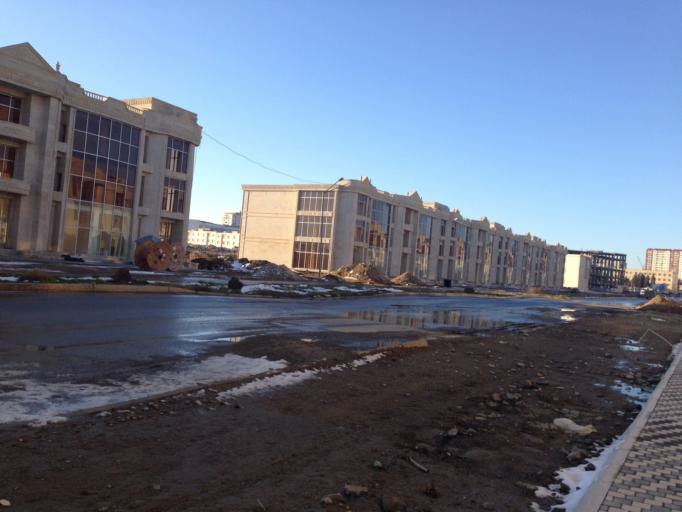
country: AZ
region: Baki
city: Baku
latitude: 40.4109
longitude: 49.8583
